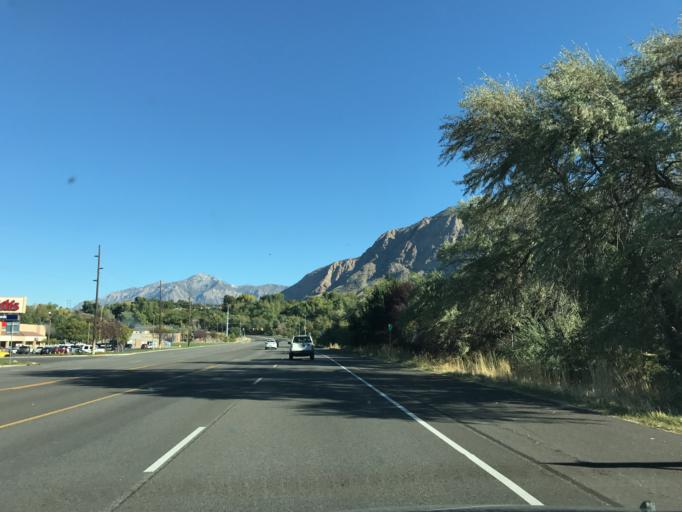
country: US
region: Utah
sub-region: Weber County
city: Ogden
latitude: 41.2393
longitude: -111.9455
